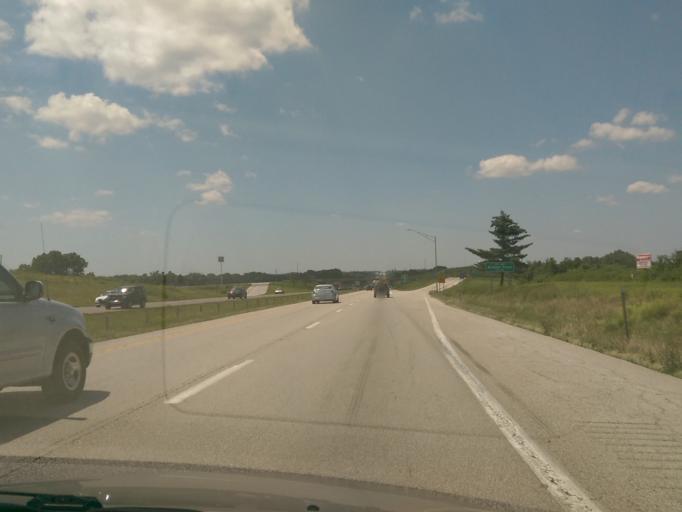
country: US
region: Missouri
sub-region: Cooper County
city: Boonville
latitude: 38.9378
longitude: -92.6868
